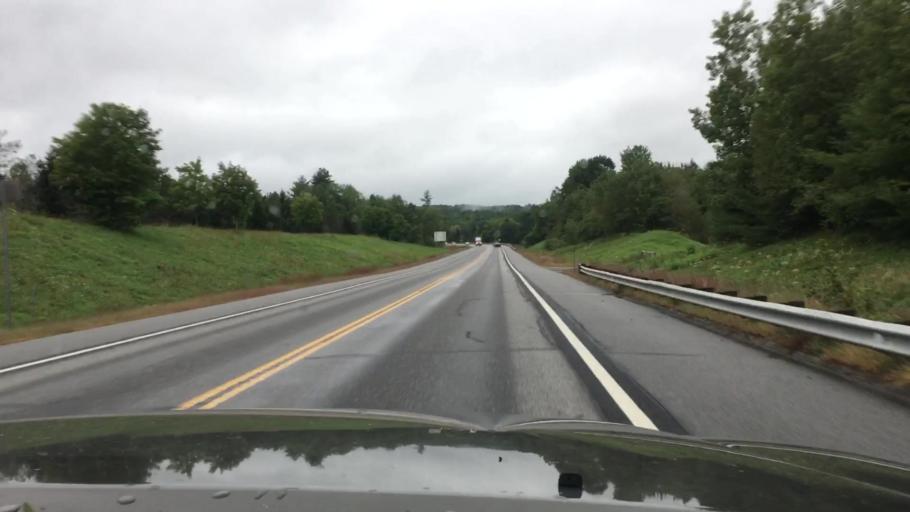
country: US
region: New Hampshire
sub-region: Hillsborough County
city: Hillsborough
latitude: 43.1175
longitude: -71.9317
